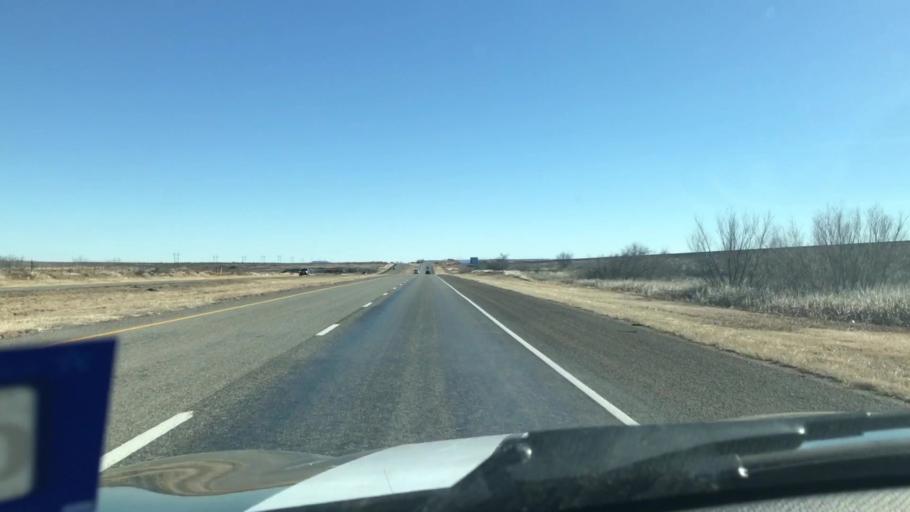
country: US
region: Texas
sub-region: Garza County
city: Post
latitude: 33.1152
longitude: -101.2757
